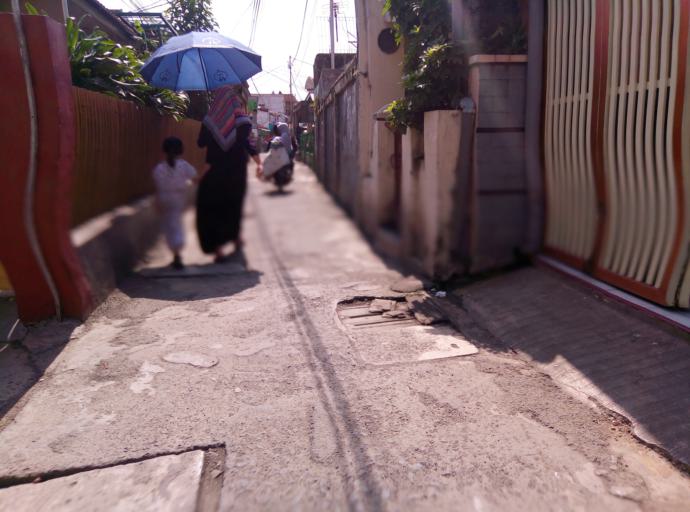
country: ID
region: West Java
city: Bandung
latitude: -6.9281
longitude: 107.6463
